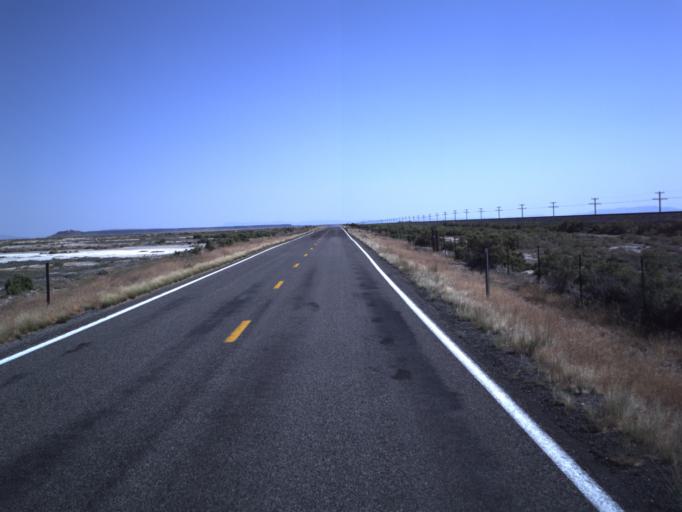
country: US
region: Utah
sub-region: Millard County
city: Delta
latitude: 39.0297
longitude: -112.7757
